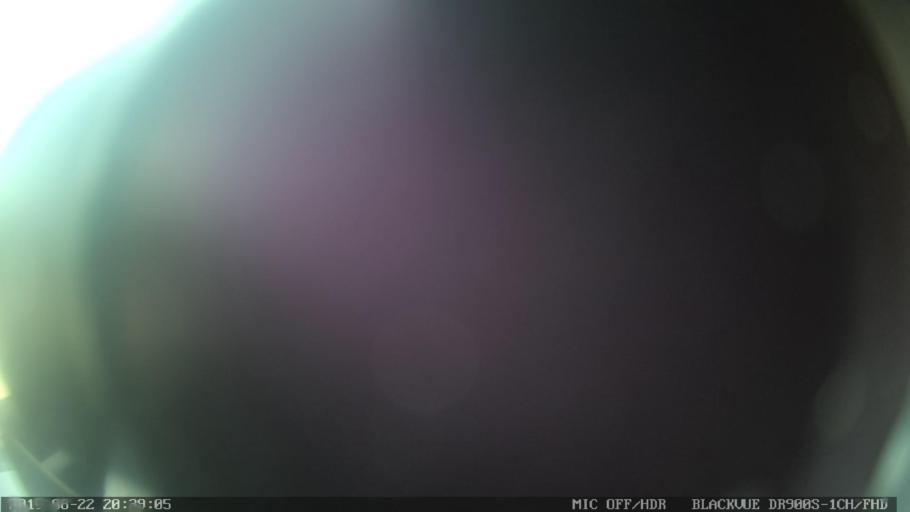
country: PT
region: Castelo Branco
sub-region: Proenca-A-Nova
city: Proenca-a-Nova
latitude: 39.6879
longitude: -7.7619
